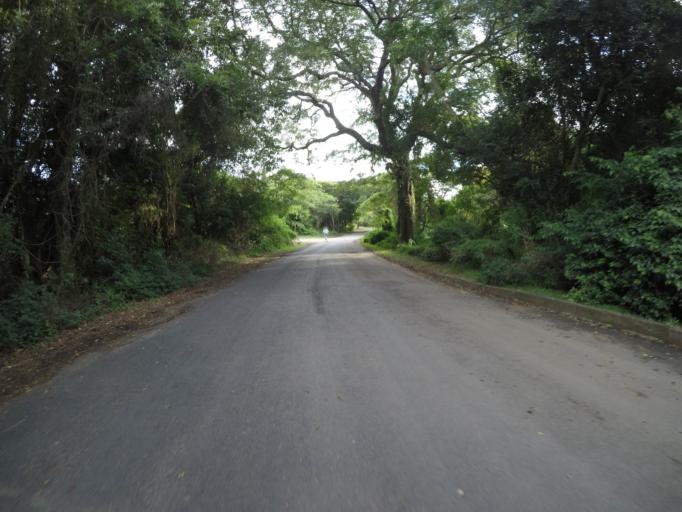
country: ZA
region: KwaZulu-Natal
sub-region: uMkhanyakude District Municipality
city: Mtubatuba
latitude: -28.3834
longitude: 32.4111
